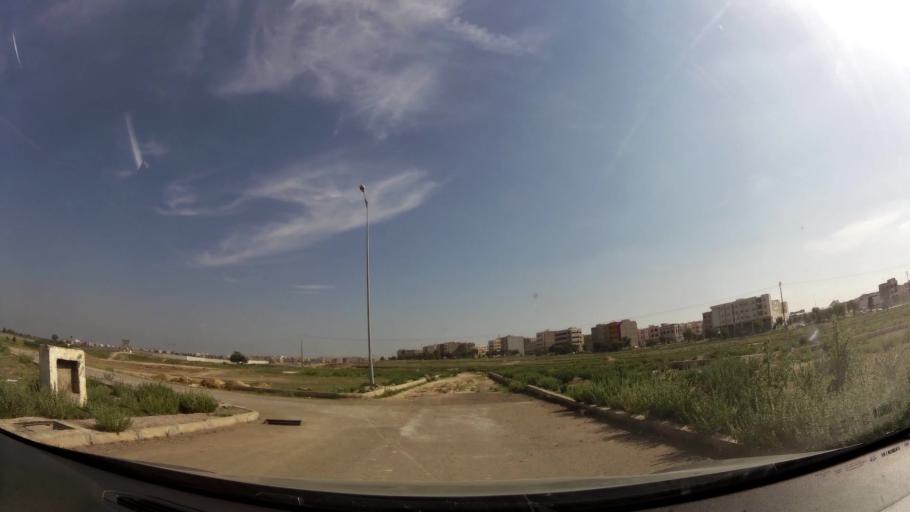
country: MA
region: Fes-Boulemane
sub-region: Fes
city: Fes
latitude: 34.0068
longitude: -5.0430
